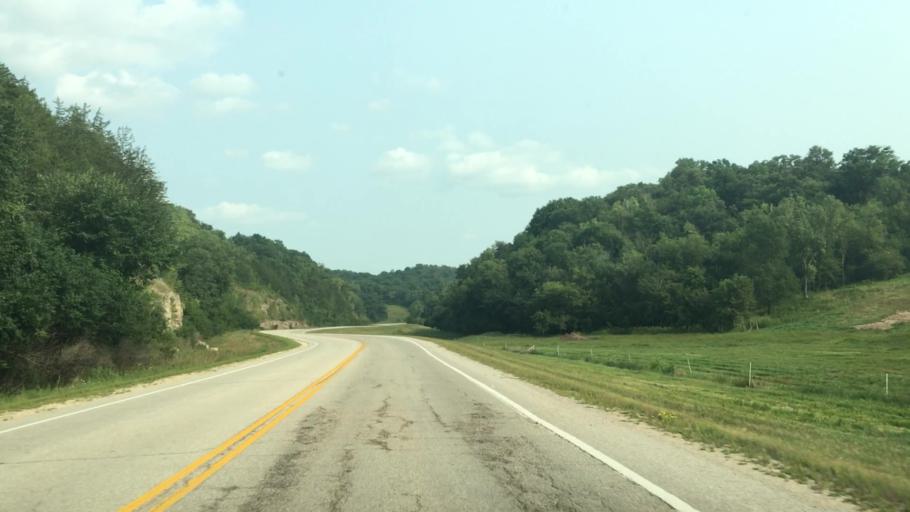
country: US
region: Minnesota
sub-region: Fillmore County
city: Preston
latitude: 43.7091
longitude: -91.9784
